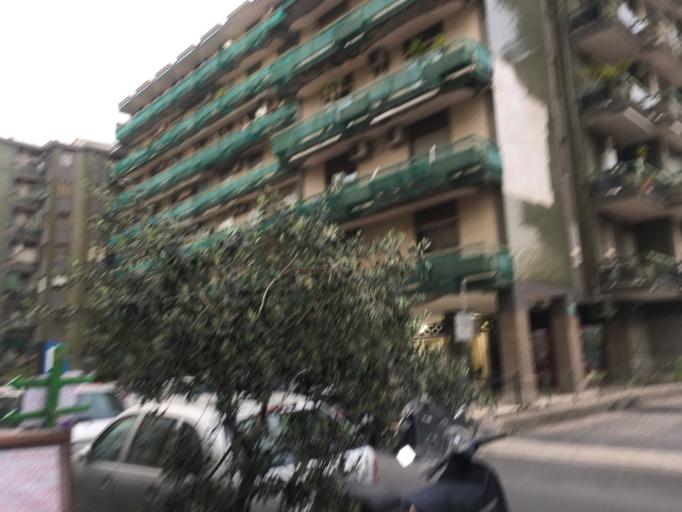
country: IT
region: Campania
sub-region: Provincia di Napoli
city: Napoli
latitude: 40.8517
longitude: 14.2260
